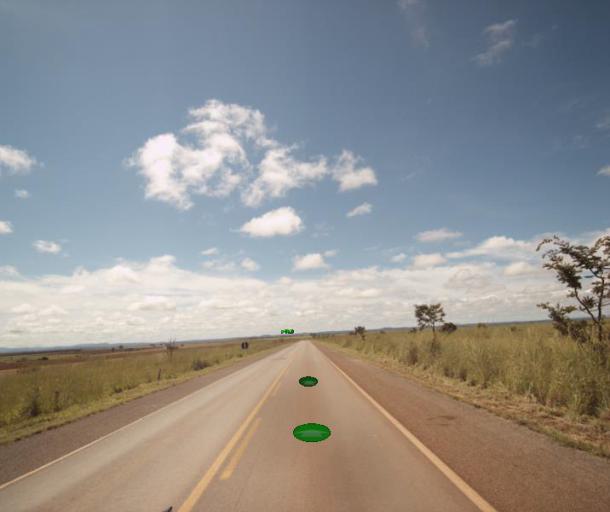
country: BR
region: Goias
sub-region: Padre Bernardo
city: Padre Bernardo
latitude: -15.1734
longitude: -48.3880
